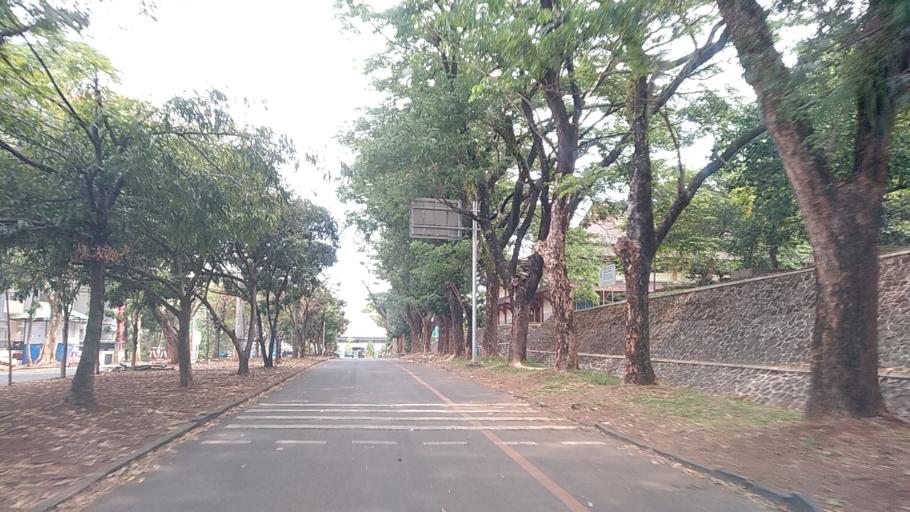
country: ID
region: Central Java
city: Semarang
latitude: -7.0506
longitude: 110.4358
